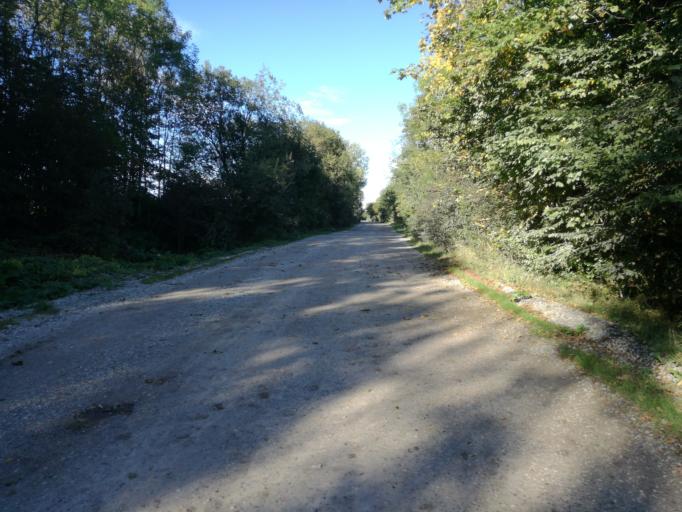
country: DE
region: Bavaria
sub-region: Upper Bavaria
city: Planegg
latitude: 48.0945
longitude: 11.4319
